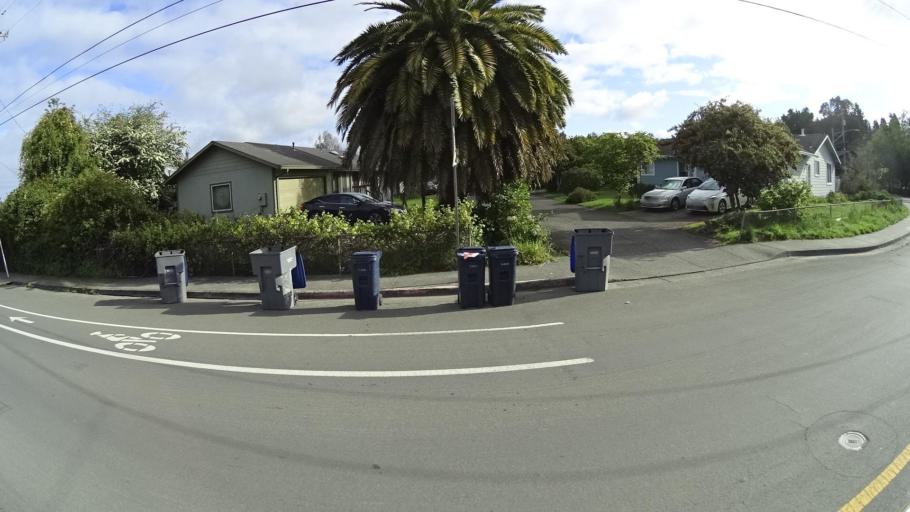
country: US
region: California
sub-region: Humboldt County
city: Arcata
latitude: 40.8891
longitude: -124.0830
